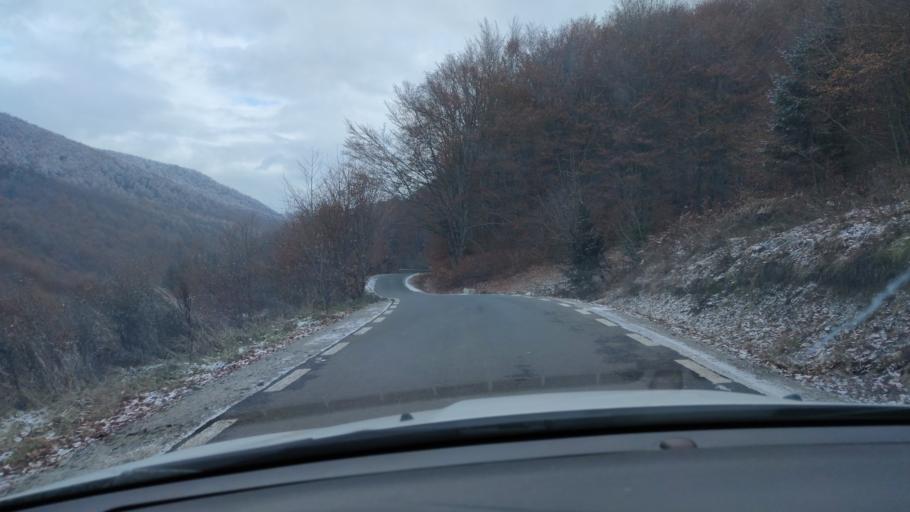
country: RO
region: Harghita
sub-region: Comuna Corund
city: Corund
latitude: 46.4799
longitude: 25.2180
